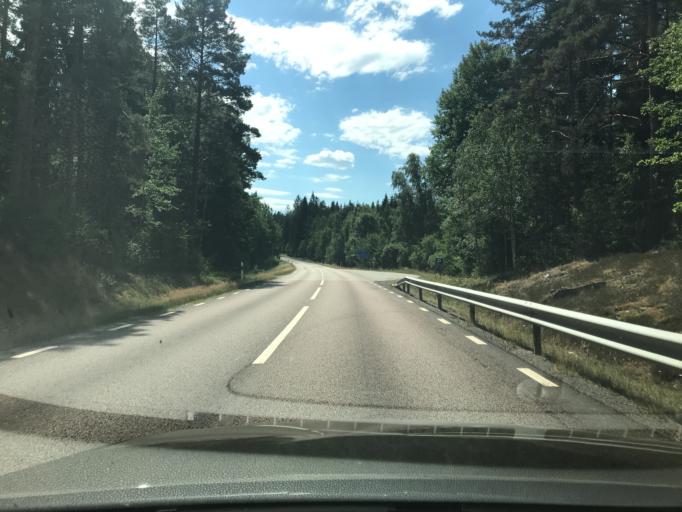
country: SE
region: Kalmar
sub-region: Hultsfreds Kommun
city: Virserum
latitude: 57.2031
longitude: 15.5160
